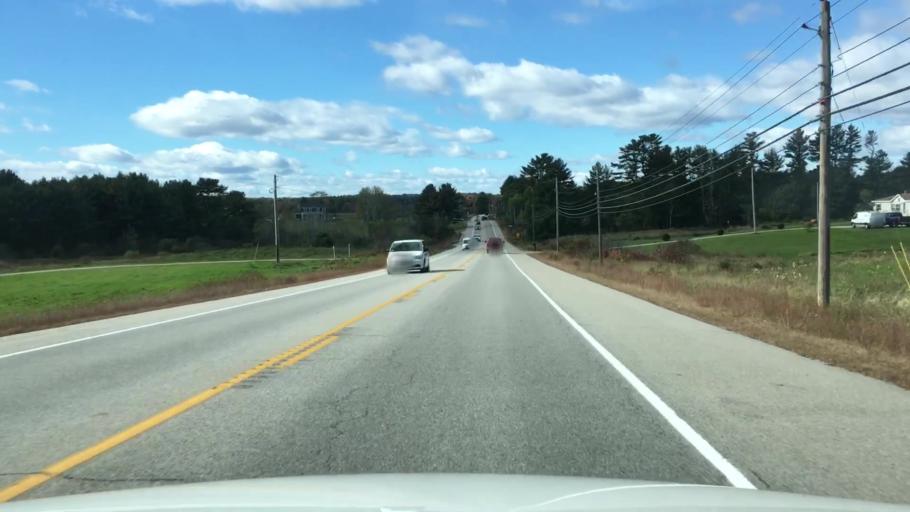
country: US
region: Maine
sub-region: York County
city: West Kennebunk
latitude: 43.4748
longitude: -70.5457
